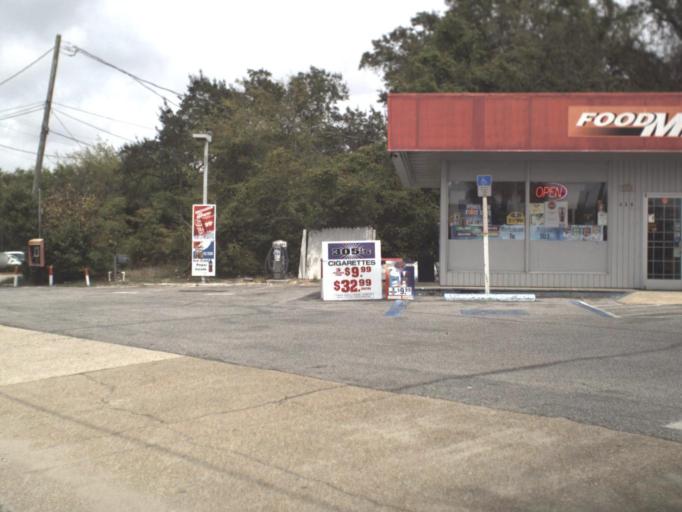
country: US
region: Florida
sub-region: Santa Rosa County
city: Gulf Breeze
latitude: 30.3668
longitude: -87.1709
